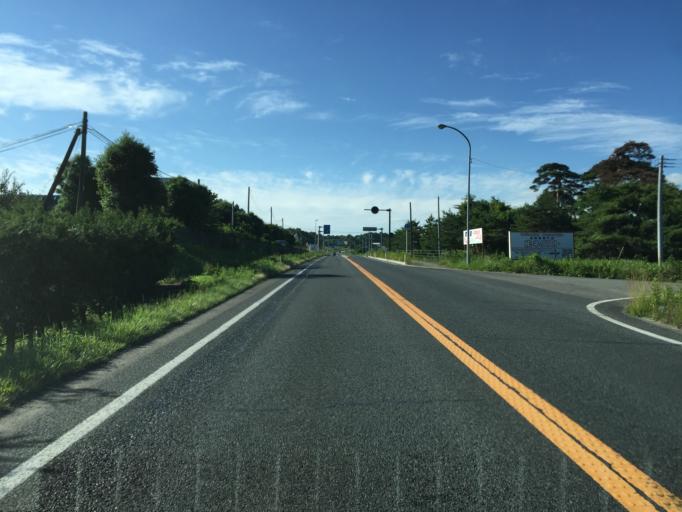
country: JP
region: Miyagi
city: Marumori
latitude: 37.7586
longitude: 140.9503
